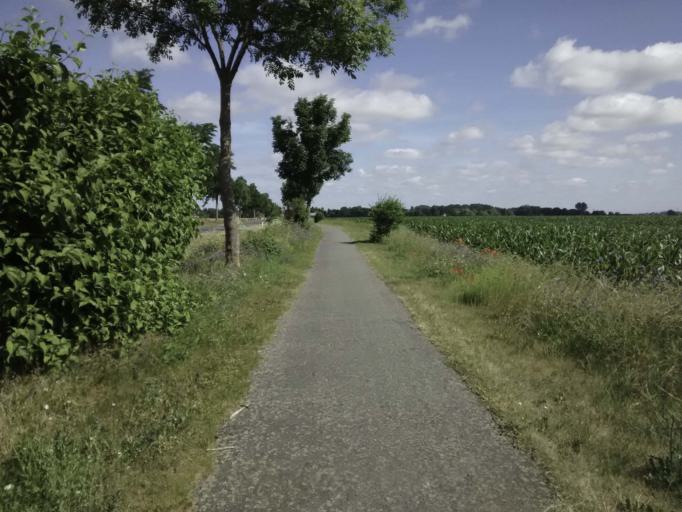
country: DE
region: Saxony-Anhalt
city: Jerichow
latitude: 52.4253
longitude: 11.9636
